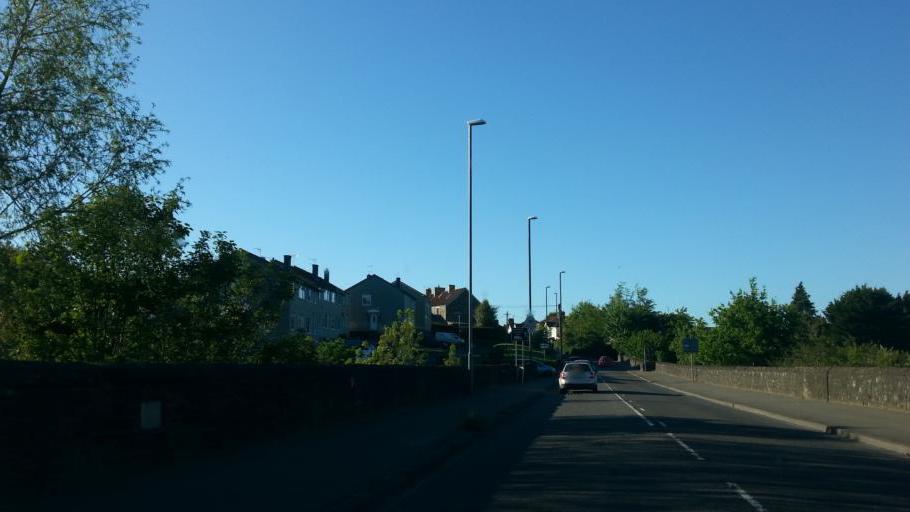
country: GB
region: England
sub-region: Bath and North East Somerset
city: Whitchurch
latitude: 51.4107
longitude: -2.5588
